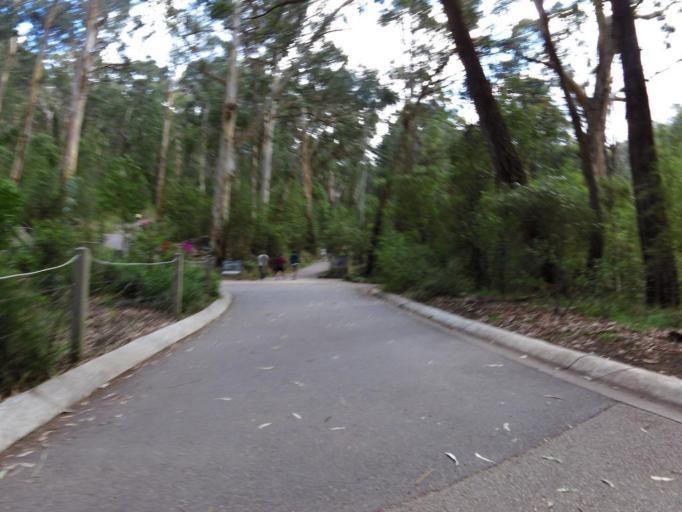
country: AU
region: Victoria
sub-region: Yarra Ranges
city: Ferny Creek
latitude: -37.8869
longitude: 145.3175
